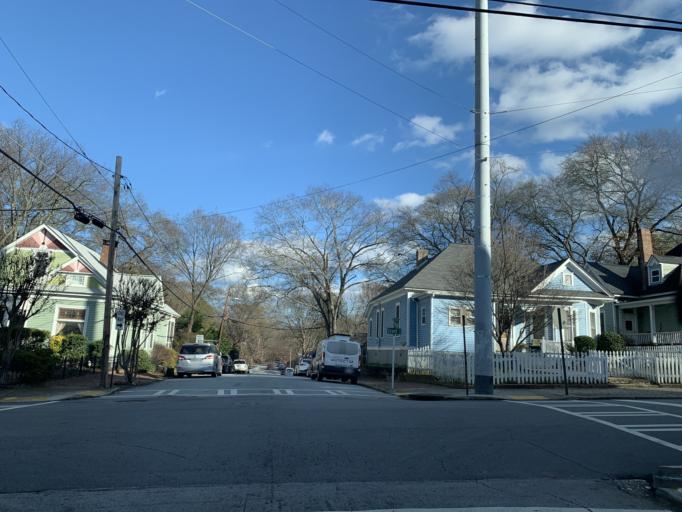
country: US
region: Georgia
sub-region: Fulton County
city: Atlanta
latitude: 33.7412
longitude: -84.3765
